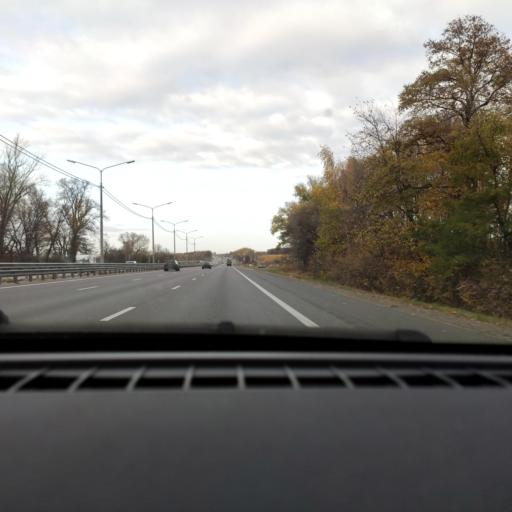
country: RU
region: Voronezj
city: Podgornoye
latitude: 51.8202
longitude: 39.2095
